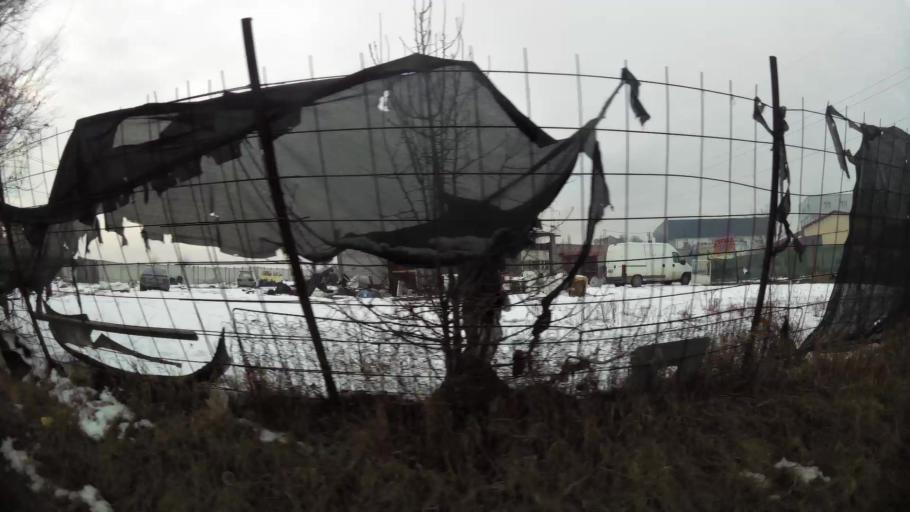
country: MK
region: Suto Orizari
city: Suto Orizare
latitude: 42.0469
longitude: 21.4279
